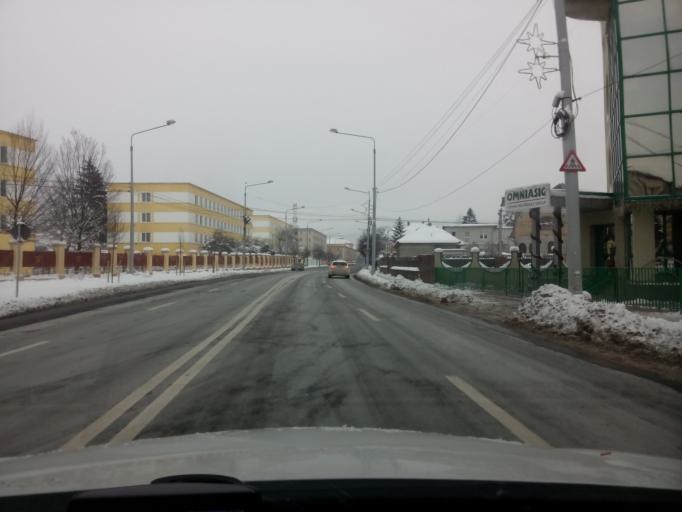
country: RO
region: Sibiu
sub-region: Municipiul Sibiu
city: Sibiu
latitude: 45.7877
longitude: 24.1549
